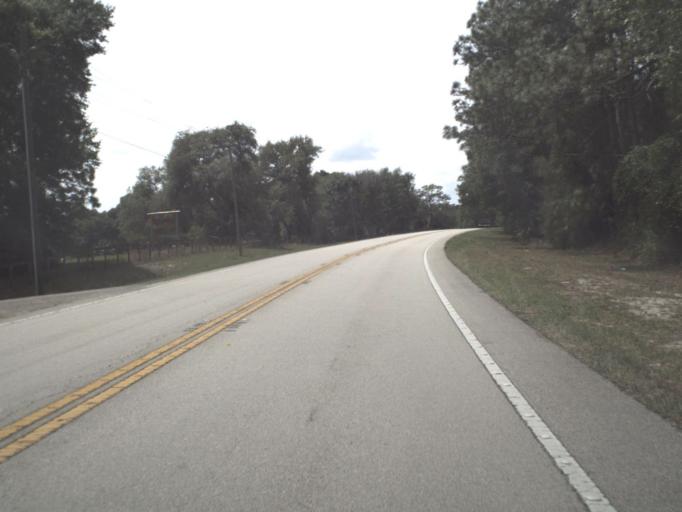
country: US
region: Florida
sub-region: Lake County
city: Lake Mack-Forest Hills
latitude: 28.9003
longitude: -81.4561
